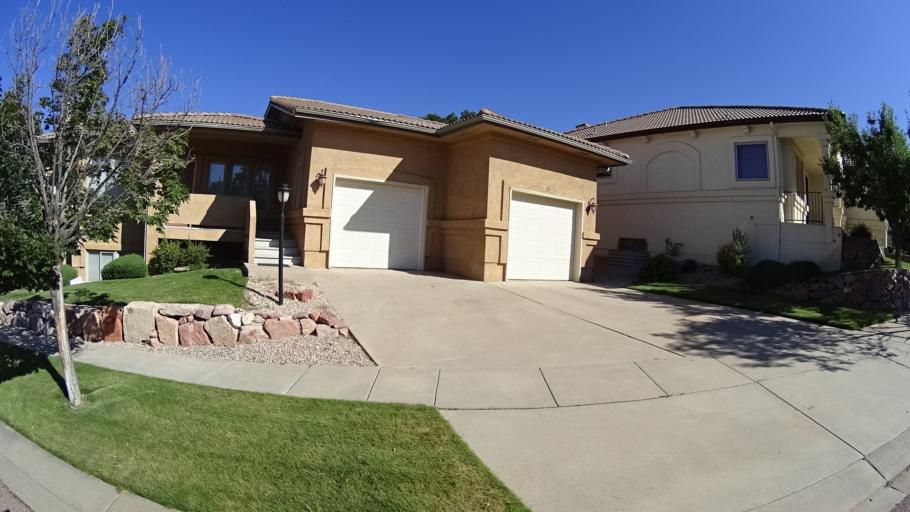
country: US
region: Colorado
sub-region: El Paso County
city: Gleneagle
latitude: 38.9729
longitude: -104.7828
